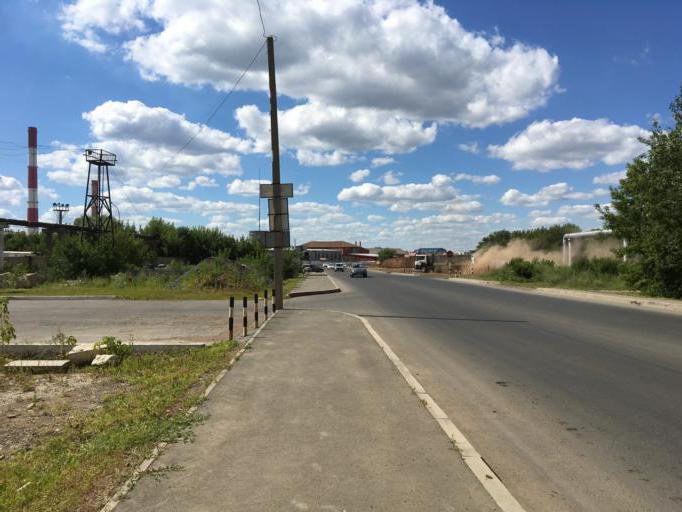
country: RU
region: Orenburg
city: Orenburg
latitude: 51.8410
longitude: 55.1111
